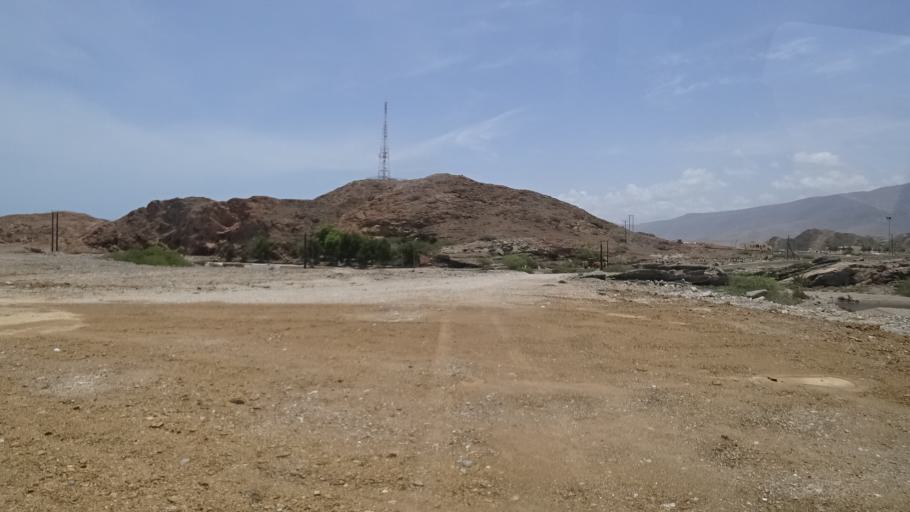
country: OM
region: Zufar
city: Salalah
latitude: 17.0003
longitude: 54.6935
